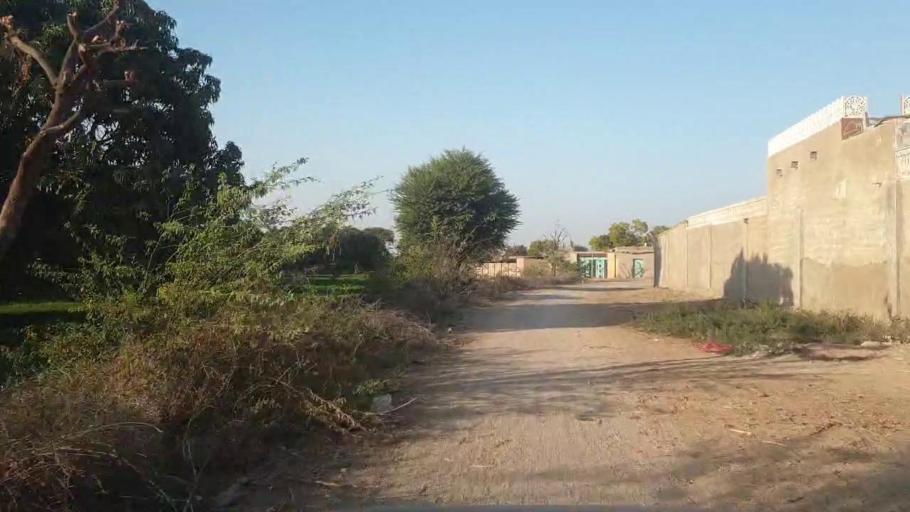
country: PK
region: Sindh
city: Chambar
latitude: 25.2667
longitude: 68.8934
